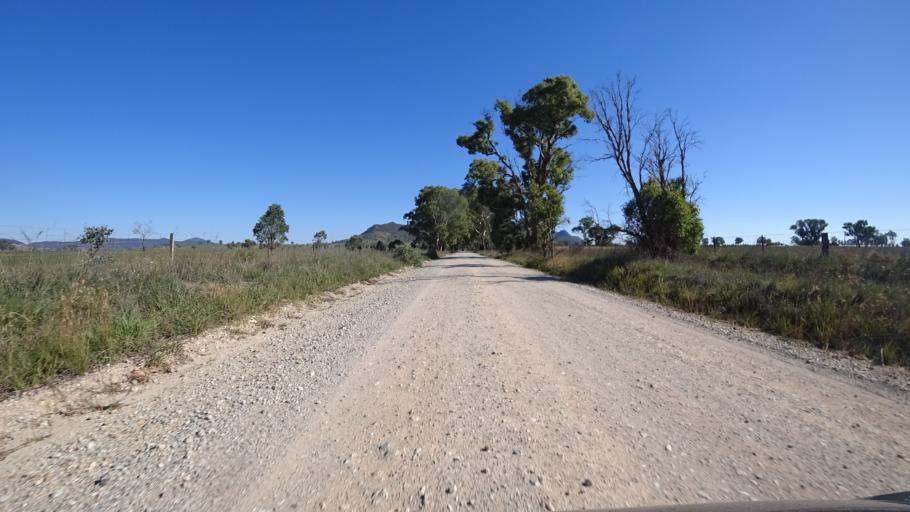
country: AU
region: New South Wales
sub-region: Mid-Western Regional
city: Kandos
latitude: -32.8225
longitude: 150.0217
